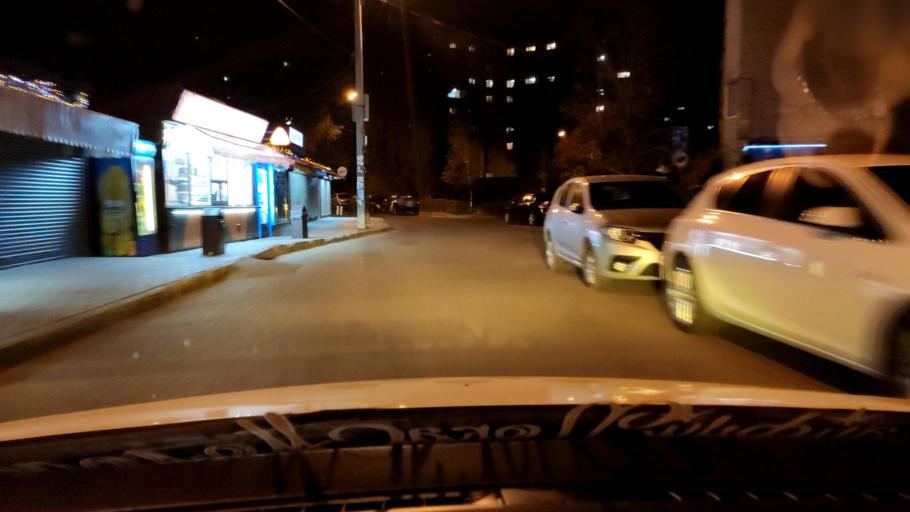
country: RU
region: Voronezj
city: Podgornoye
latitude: 51.7193
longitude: 39.1692
